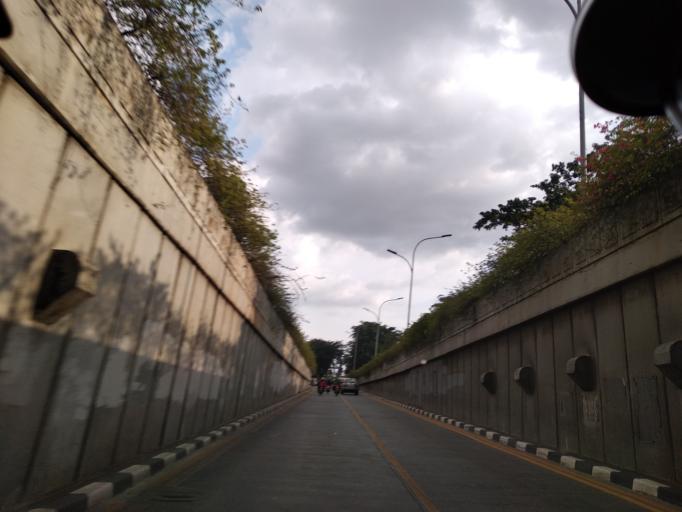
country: ID
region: Jakarta Raya
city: Jakarta
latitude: -6.2398
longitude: 106.7830
